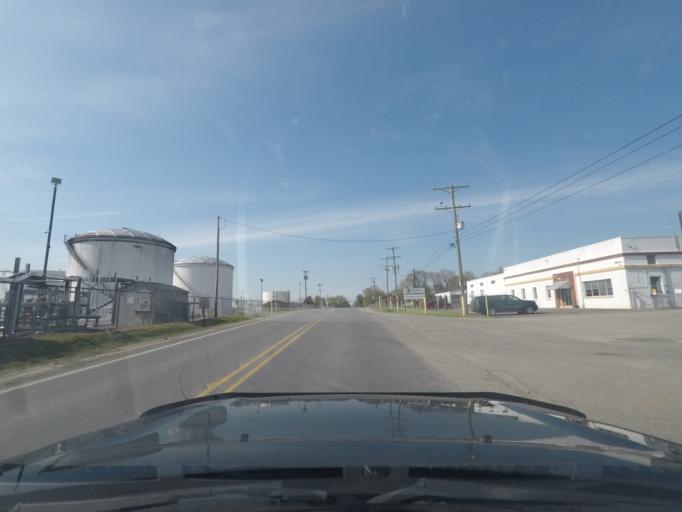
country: US
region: Michigan
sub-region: Berrien County
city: Niles
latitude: 41.7853
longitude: -86.2548
